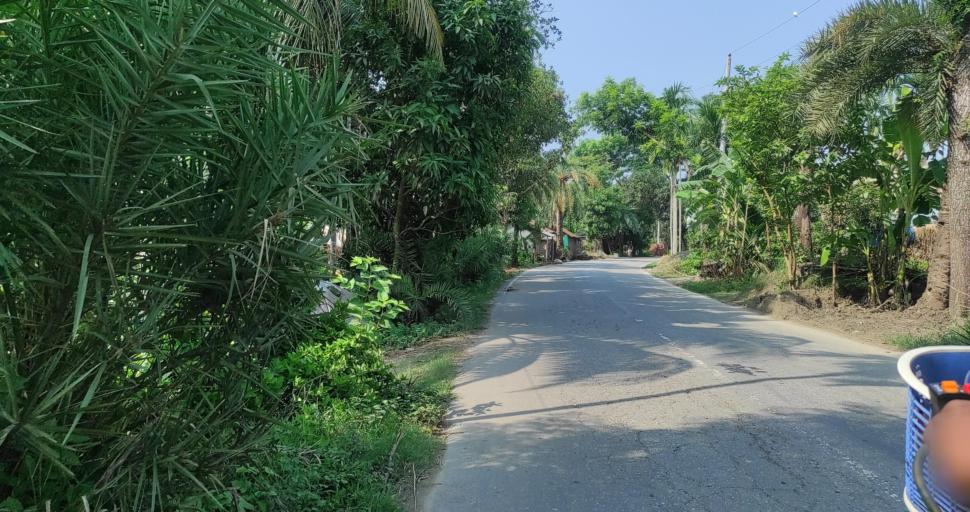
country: BD
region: Rajshahi
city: Ishurdi
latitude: 24.2584
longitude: 89.0484
